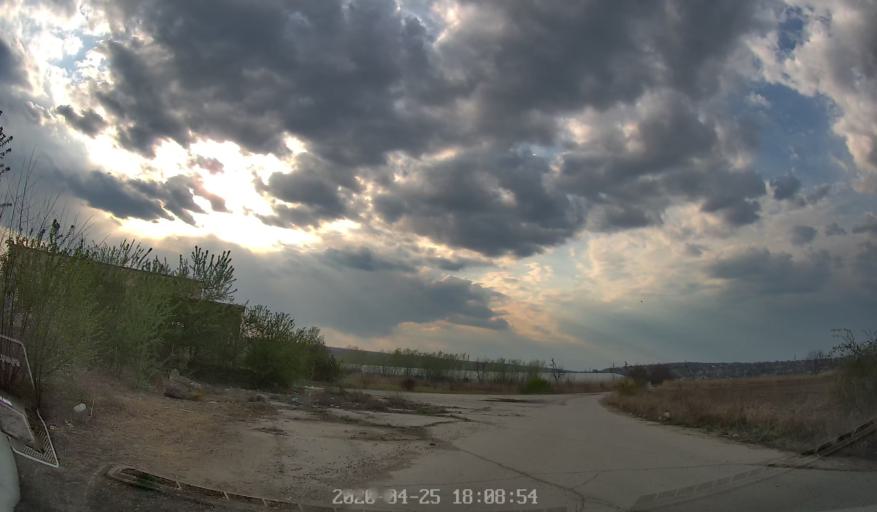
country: MD
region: Chisinau
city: Vadul lui Voda
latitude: 47.1297
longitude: 29.0814
